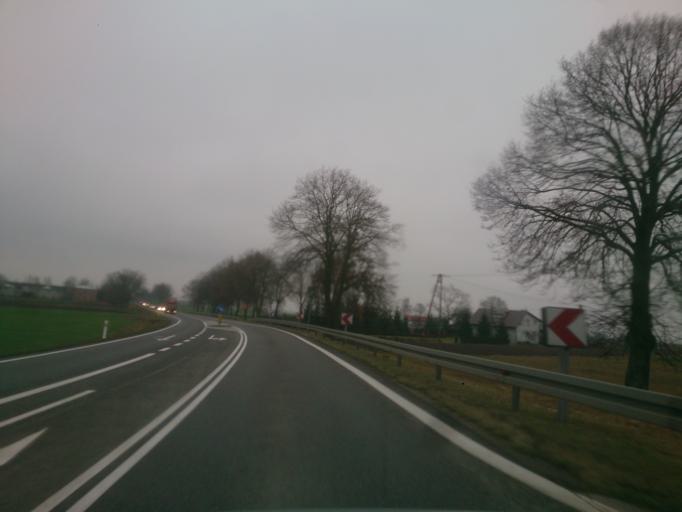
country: PL
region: Masovian Voivodeship
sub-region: Powiat plonski
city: Dzierzaznia
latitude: 52.6248
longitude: 20.2577
